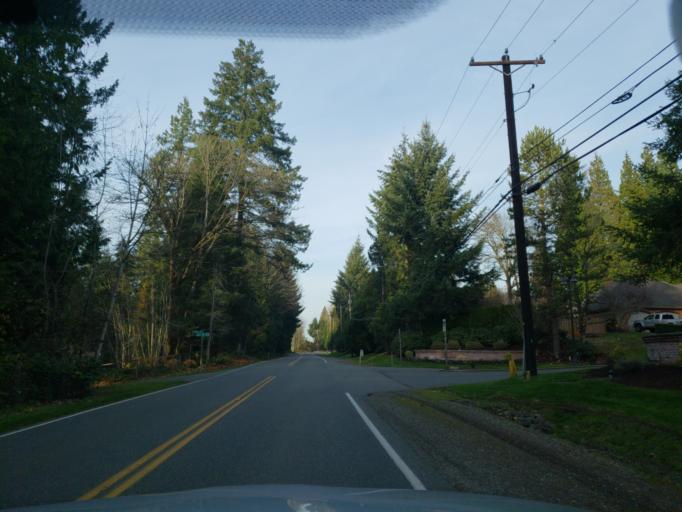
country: US
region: Washington
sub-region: Snohomish County
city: Maltby
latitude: 47.7909
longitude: -122.1331
